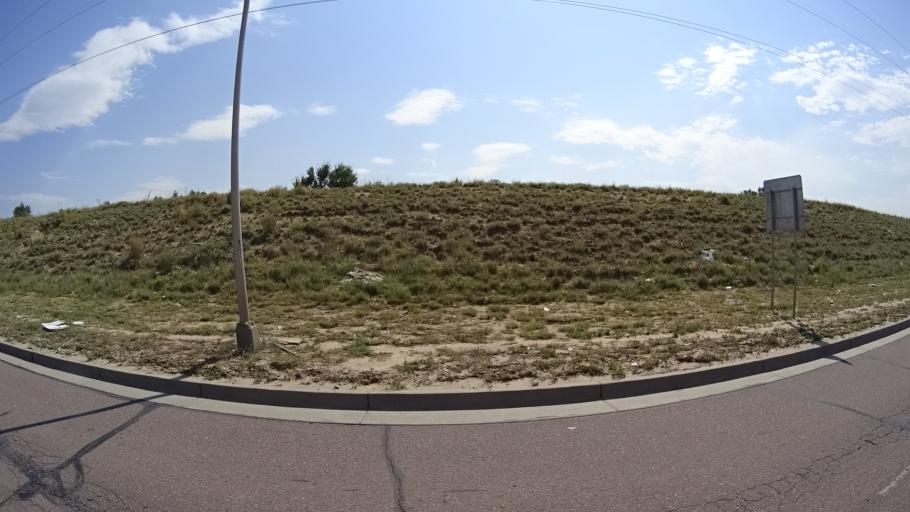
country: US
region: Colorado
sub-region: El Paso County
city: Stratmoor
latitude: 38.7757
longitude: -104.7574
